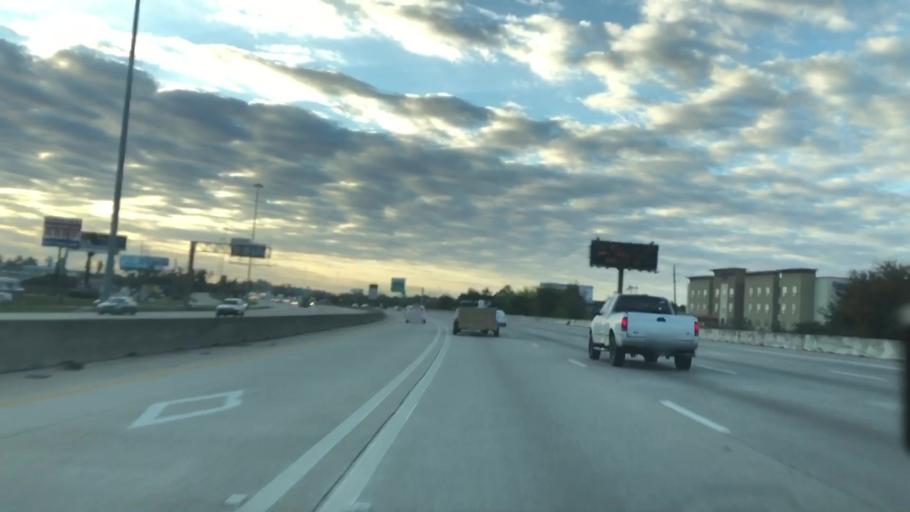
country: US
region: Texas
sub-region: Montgomery County
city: Oak Ridge North
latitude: 30.1200
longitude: -95.4418
